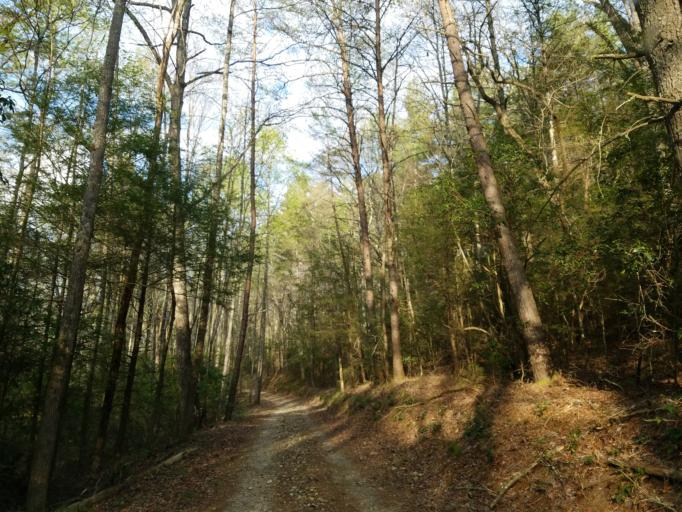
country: US
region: Georgia
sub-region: Fannin County
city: Blue Ridge
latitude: 34.7225
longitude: -84.2043
